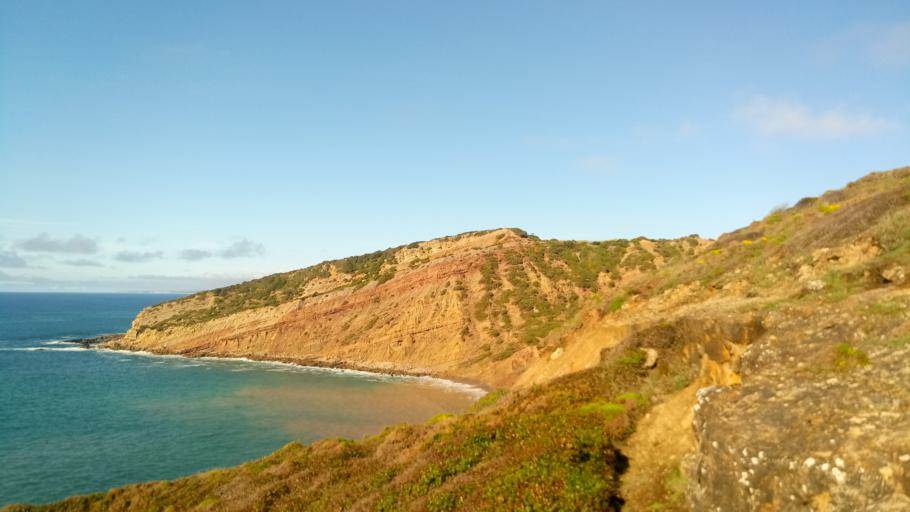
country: PT
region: Leiria
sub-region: Caldas da Rainha
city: Caldas da Rainha
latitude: 39.4954
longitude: -9.1739
